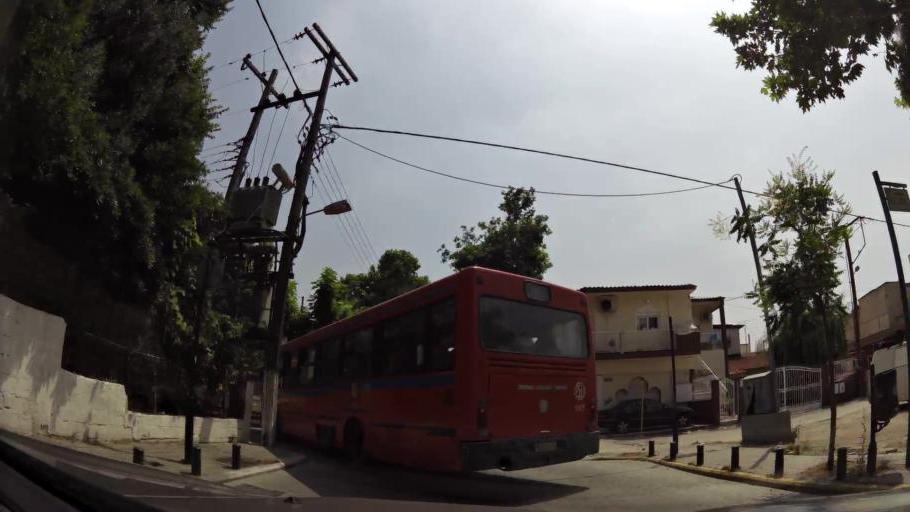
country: GR
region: Central Macedonia
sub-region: Nomos Thessalonikis
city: Menemeni
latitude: 40.6591
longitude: 22.8975
